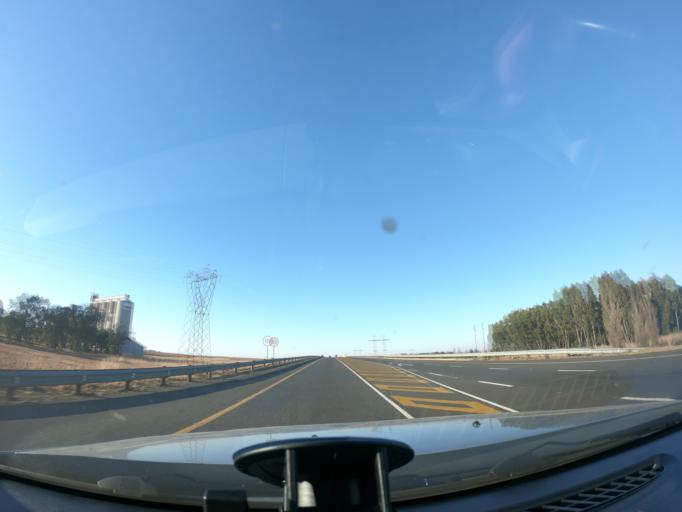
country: ZA
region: Mpumalanga
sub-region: Gert Sibande District Municipality
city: Breyten
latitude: -26.3355
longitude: 29.8703
